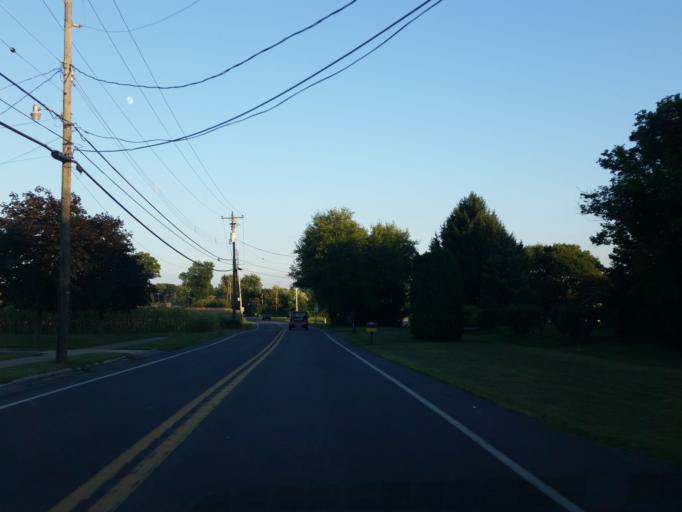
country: US
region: Pennsylvania
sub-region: Lebanon County
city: Sand Hill
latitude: 40.3775
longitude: -76.4423
